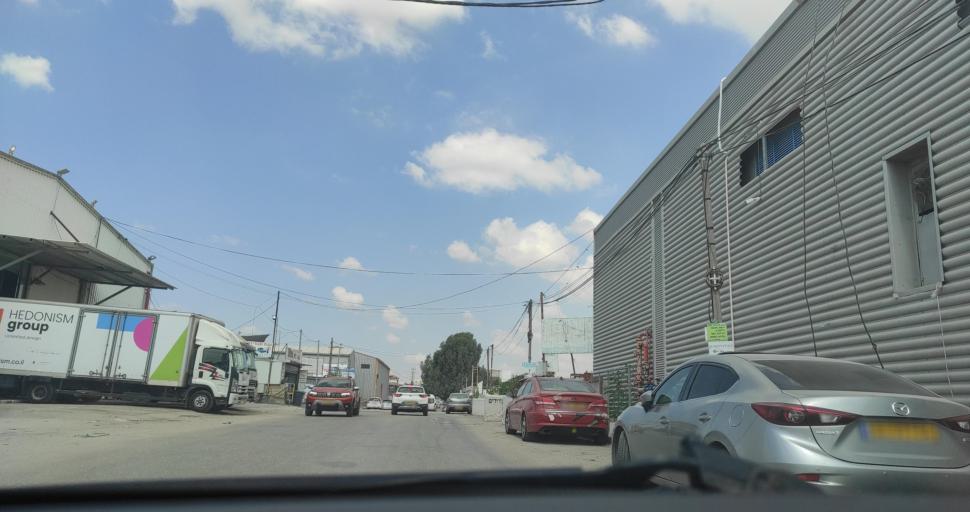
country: IL
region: Central District
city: Rosh Ha'Ayin
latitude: 32.1135
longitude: 34.9559
